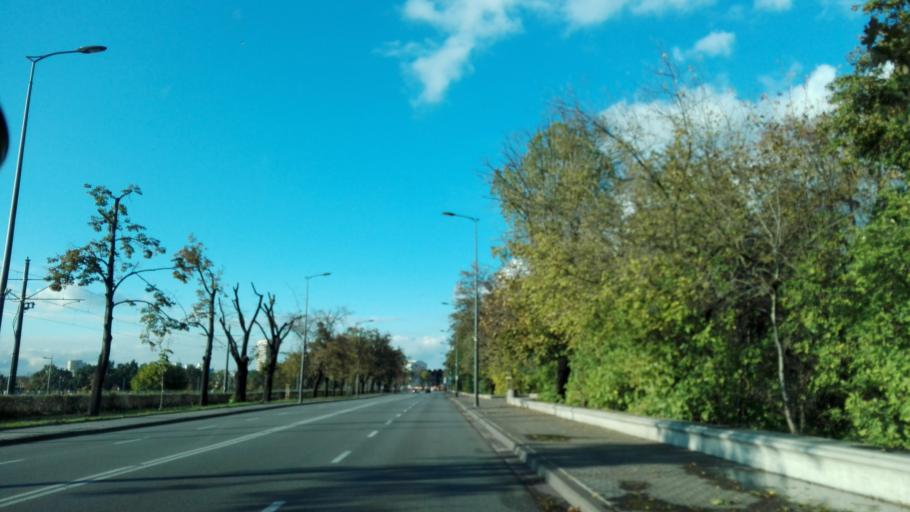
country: PL
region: Masovian Voivodeship
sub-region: Warszawa
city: Praga Polnoc
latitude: 52.2434
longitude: 21.0491
